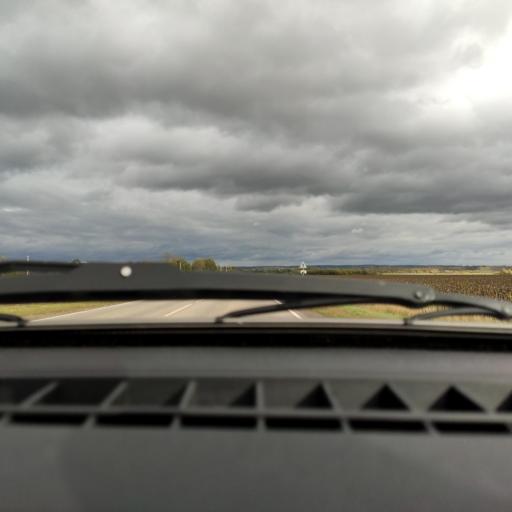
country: RU
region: Bashkortostan
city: Rayevskiy
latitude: 54.0137
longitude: 54.8605
